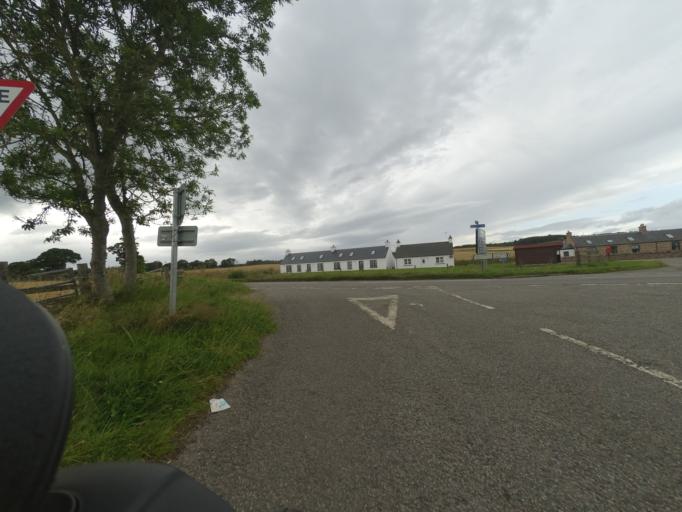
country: GB
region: Scotland
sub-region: Highland
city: Muir of Ord
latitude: 57.5132
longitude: -4.3930
